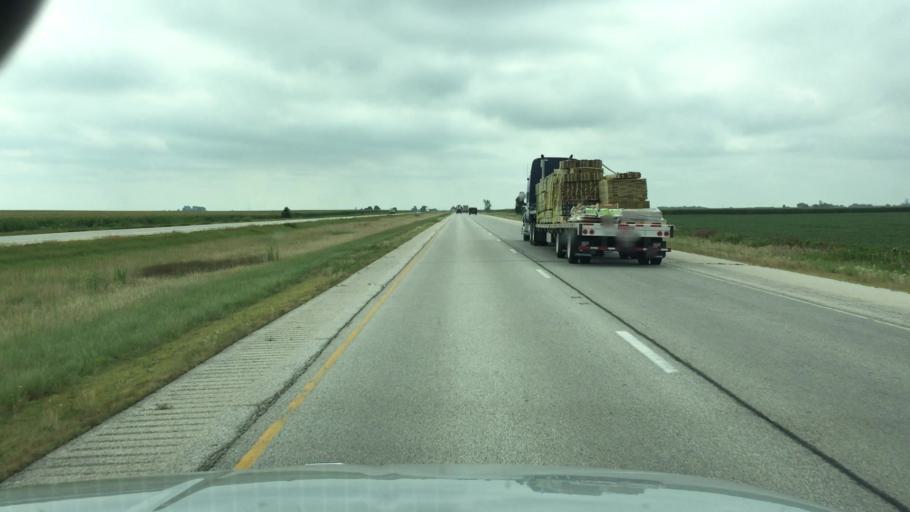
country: US
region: Illinois
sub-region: Knox County
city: Galesburg
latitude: 41.0516
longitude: -90.3342
